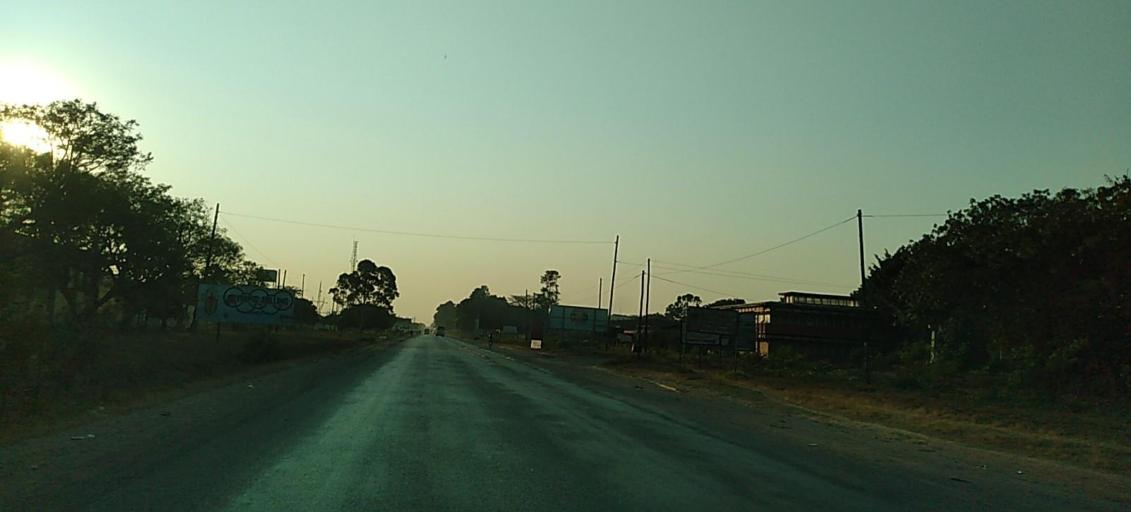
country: ZM
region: Copperbelt
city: Ndola
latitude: -13.0155
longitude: 28.6625
